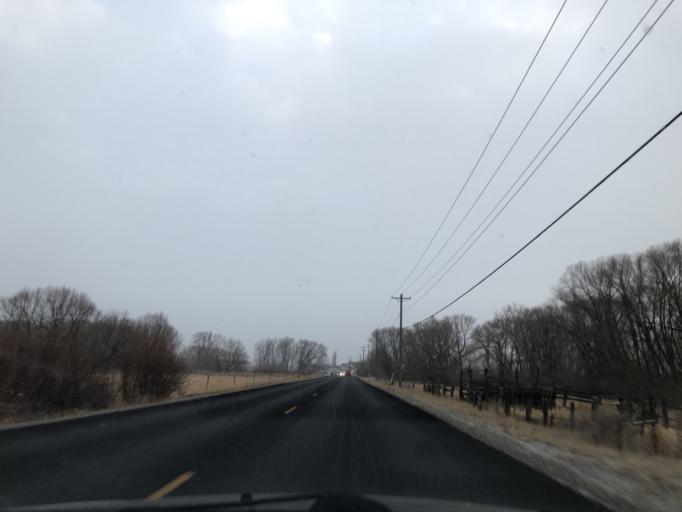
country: US
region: Utah
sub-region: Cache County
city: Logan
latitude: 41.7089
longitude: -111.8531
